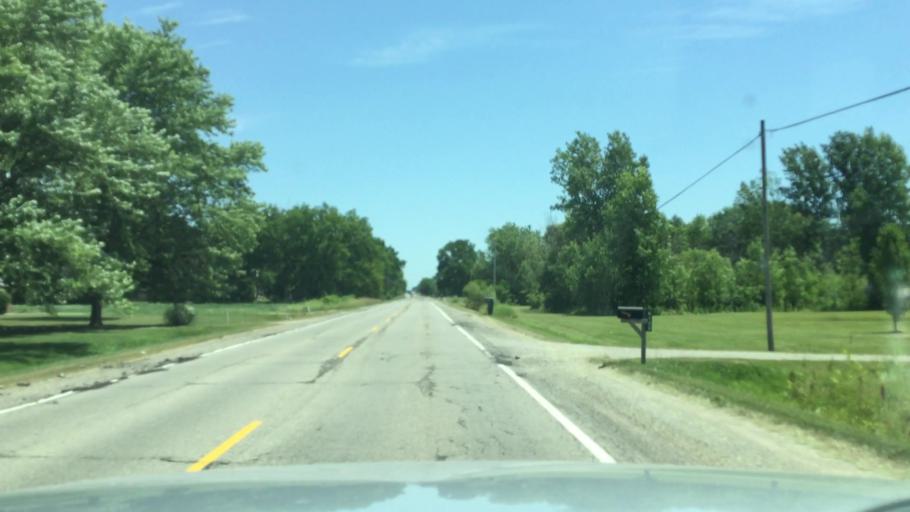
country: US
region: Michigan
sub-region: Genesee County
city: Swartz Creek
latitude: 42.9428
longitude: -83.7962
